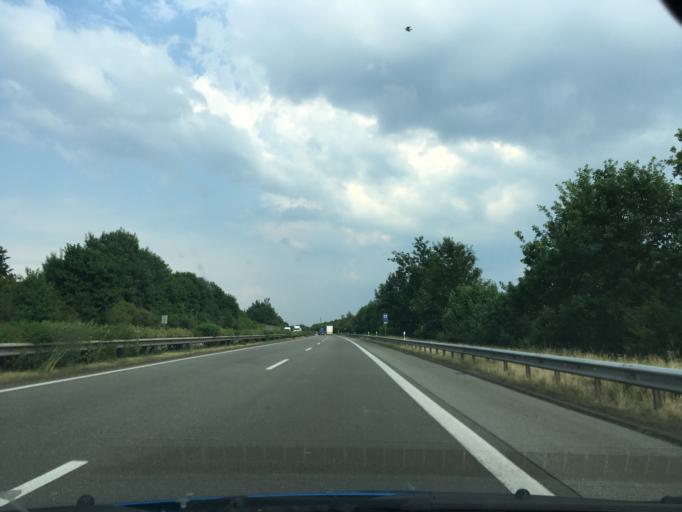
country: DE
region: Lower Saxony
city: Winsen
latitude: 53.3403
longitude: 10.1892
